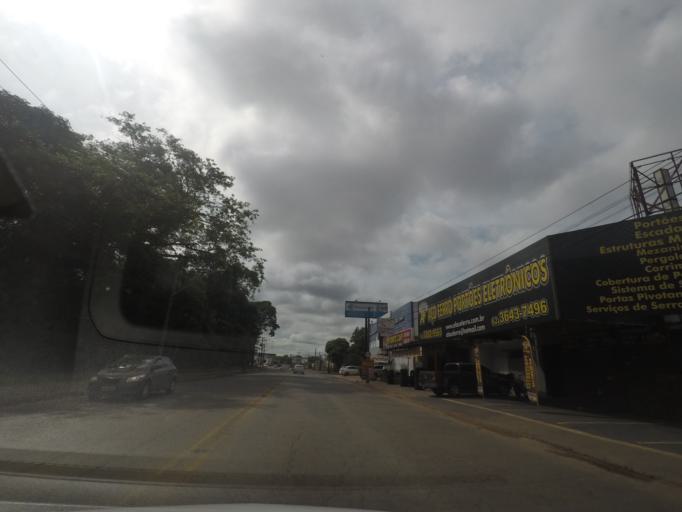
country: BR
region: Goias
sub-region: Goiania
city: Goiania
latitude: -16.7268
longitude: -49.2470
